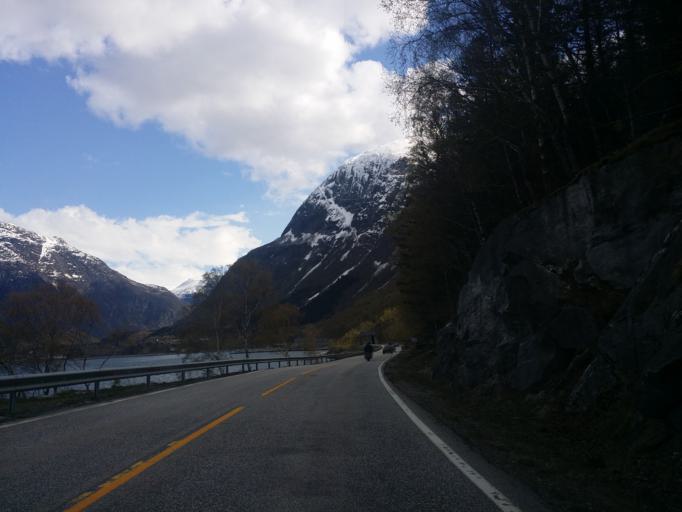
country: NO
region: Hordaland
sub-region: Eidfjord
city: Eidfjord
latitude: 60.4728
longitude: 7.0435
